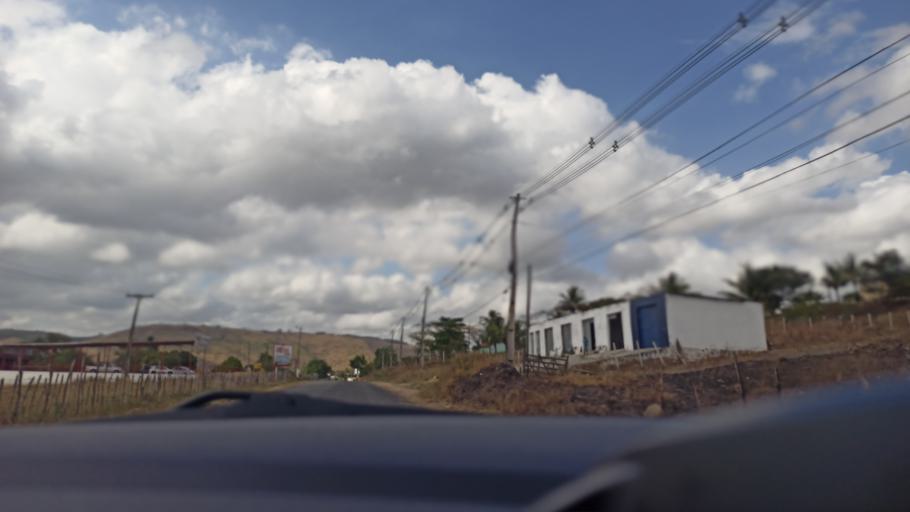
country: BR
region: Pernambuco
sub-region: Timbauba
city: Timbauba
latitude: -7.5075
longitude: -35.3010
